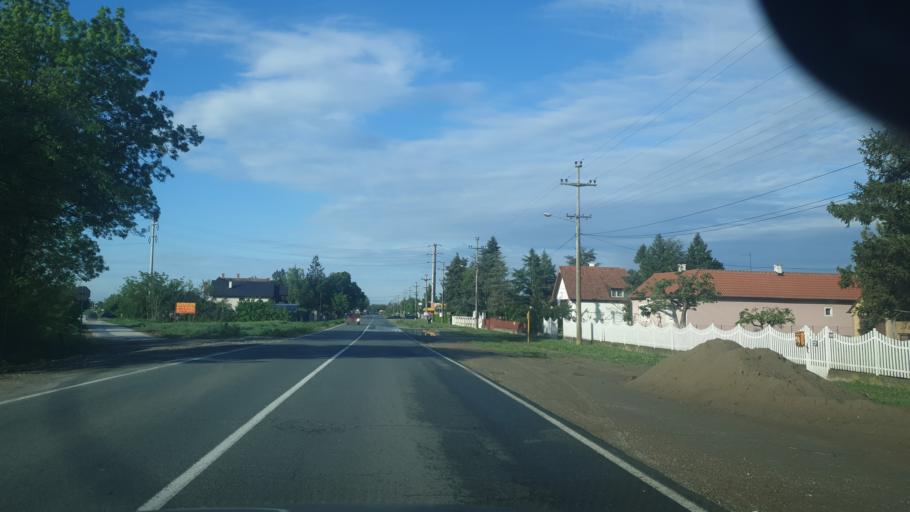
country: RS
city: Zvecka
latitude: 44.6228
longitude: 20.1738
